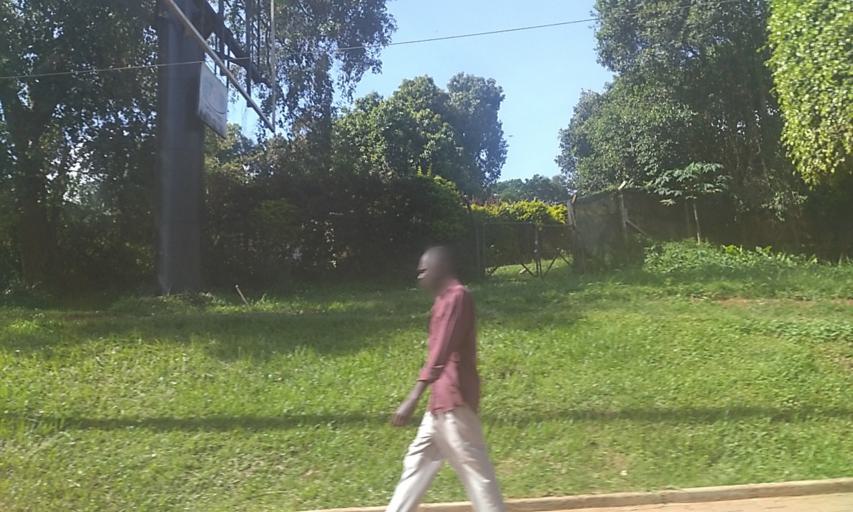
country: UG
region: Central Region
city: Kampala Central Division
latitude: 0.3370
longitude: 32.5797
